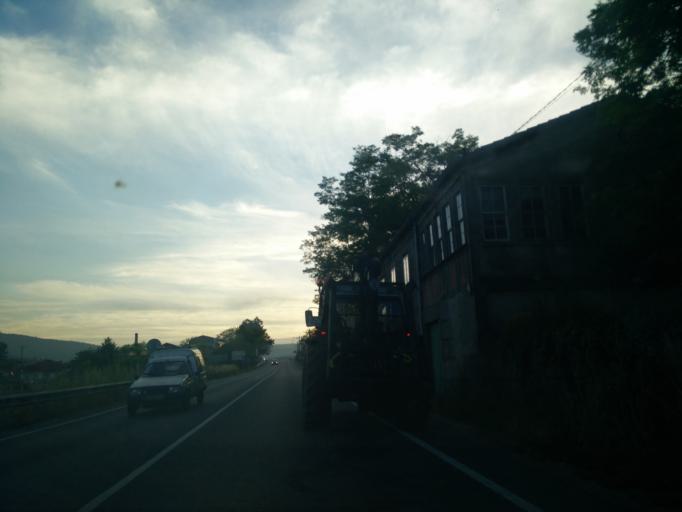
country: ES
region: Galicia
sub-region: Provincia de Pontevedra
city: Ponteareas
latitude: 42.1781
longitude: -8.5135
